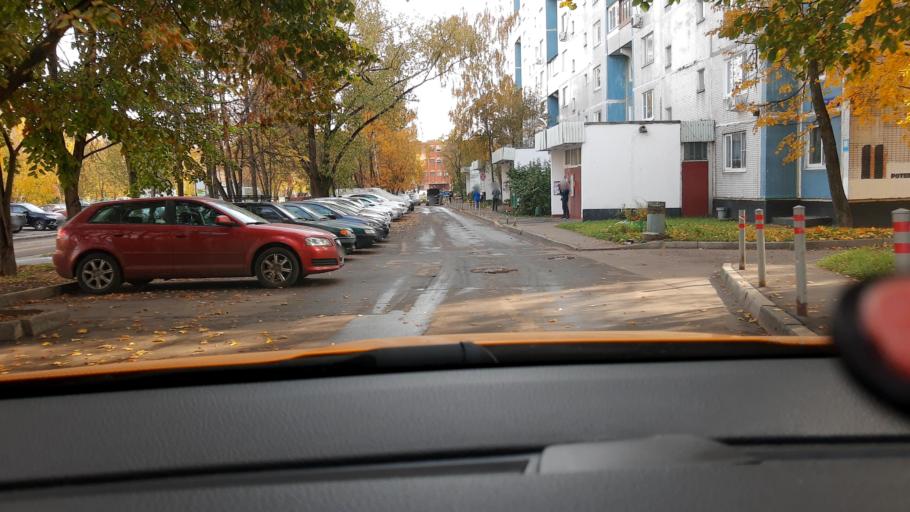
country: RU
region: Moscow
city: Babushkin
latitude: 55.8768
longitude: 37.7251
